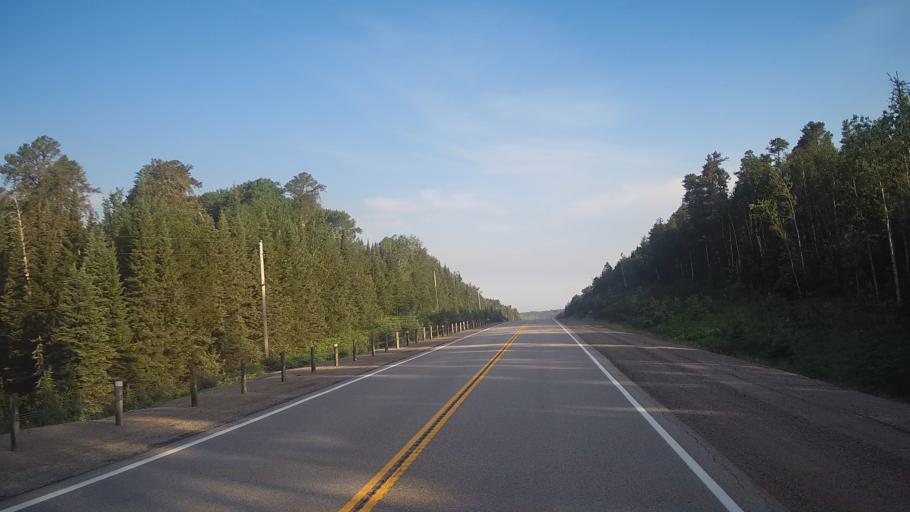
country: CA
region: Ontario
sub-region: Rainy River District
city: Atikokan
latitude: 49.3776
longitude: -91.5812
